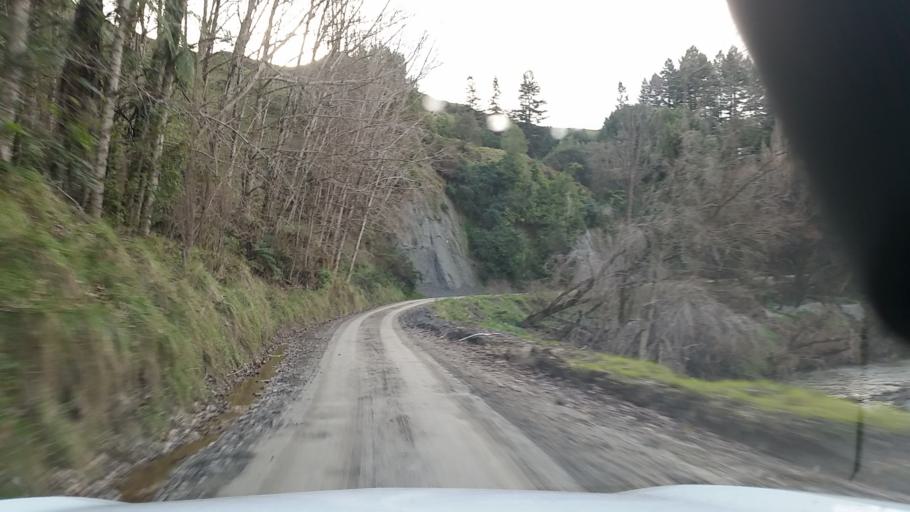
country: NZ
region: Taranaki
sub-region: South Taranaki District
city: Patea
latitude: -39.5638
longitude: 174.8043
